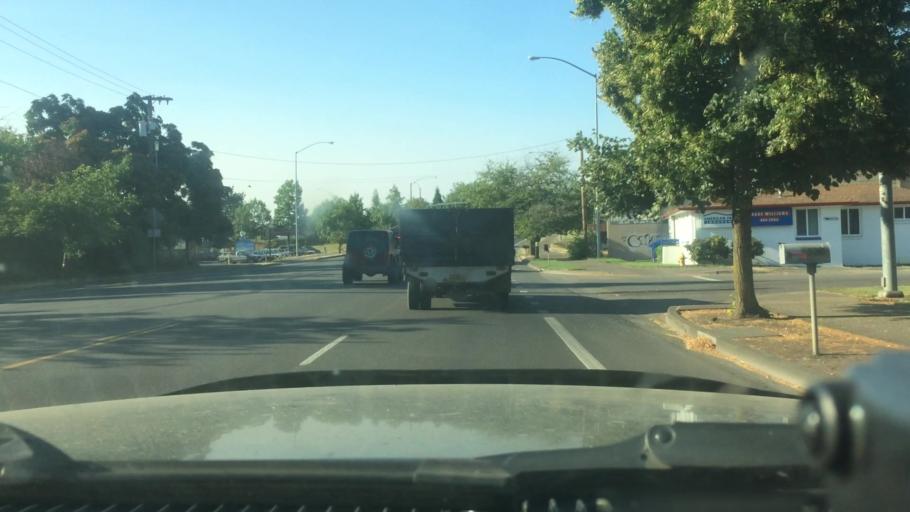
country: US
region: Oregon
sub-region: Lane County
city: Eugene
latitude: 44.0657
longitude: -123.1176
